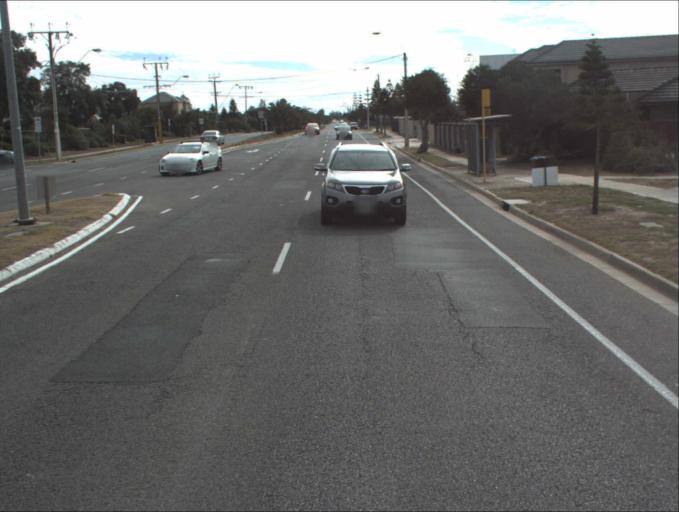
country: AU
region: South Australia
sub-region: Charles Sturt
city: West Lakes Shore
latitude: -34.8652
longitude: 138.4799
